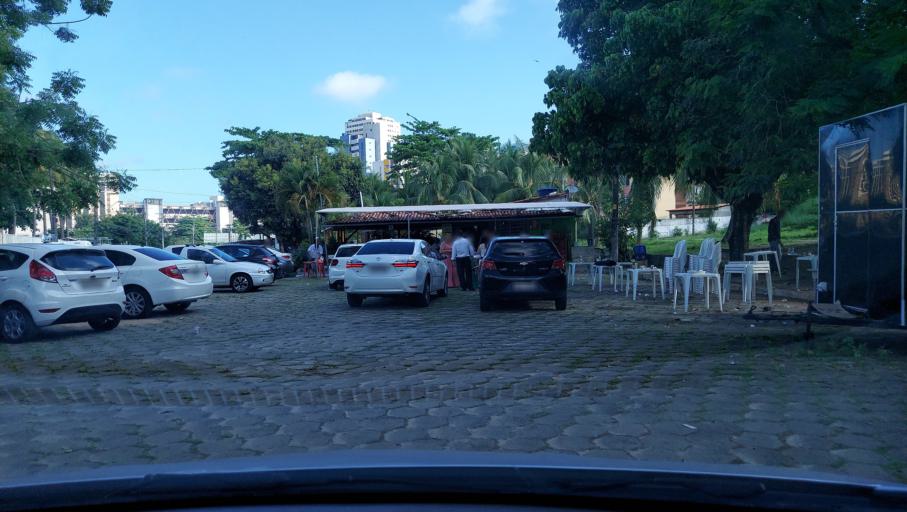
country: BR
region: Bahia
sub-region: Salvador
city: Salvador
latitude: -12.9797
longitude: -38.4444
